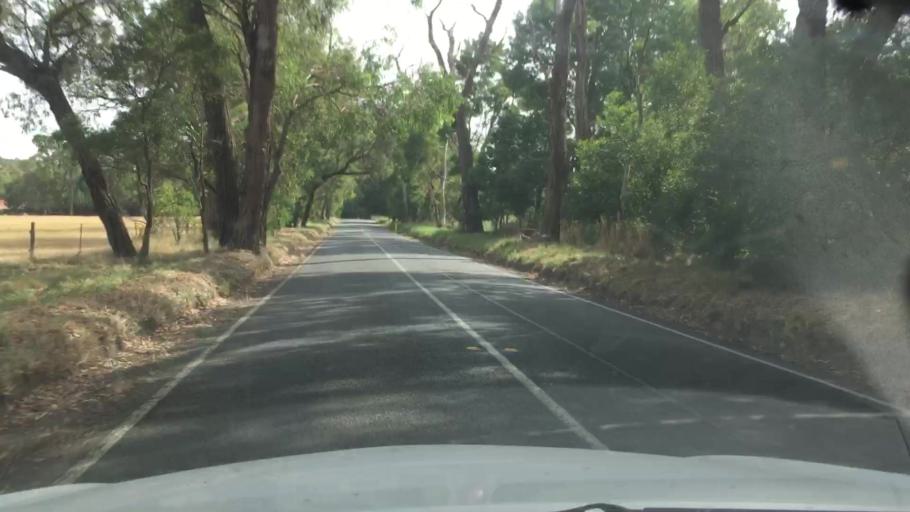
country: AU
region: Victoria
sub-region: Yarra Ranges
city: Woori Yallock
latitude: -37.8199
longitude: 145.4965
